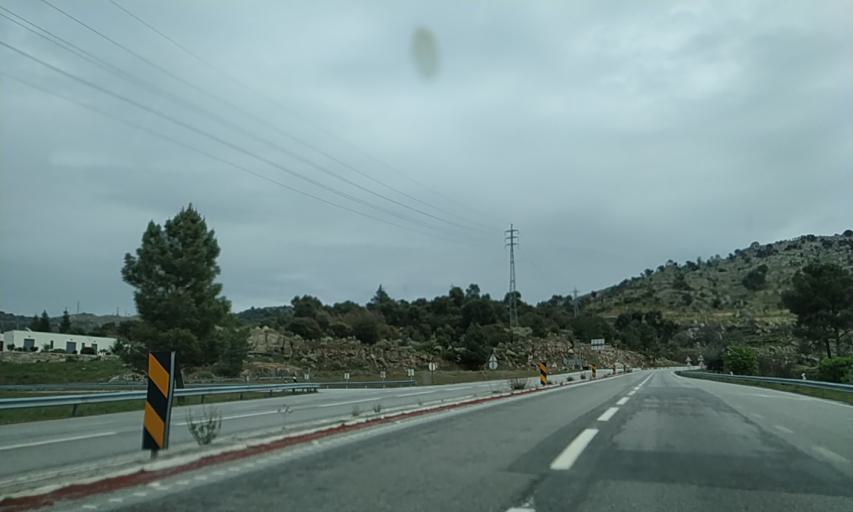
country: PT
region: Guarda
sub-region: Guarda
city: Guarda
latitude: 40.6183
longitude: -7.2850
